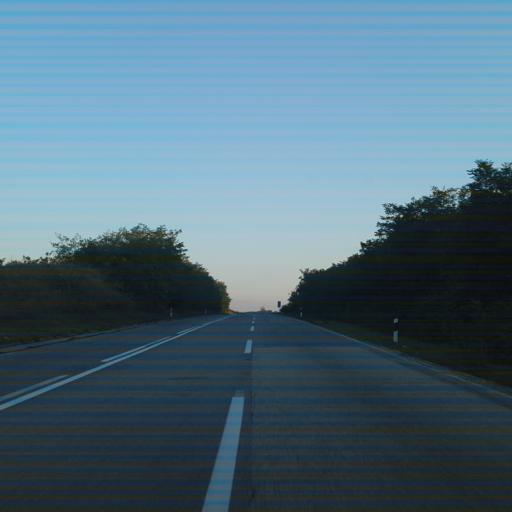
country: RS
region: Central Serbia
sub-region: Zajecarski Okrug
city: Zajecar
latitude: 43.9971
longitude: 22.3020
